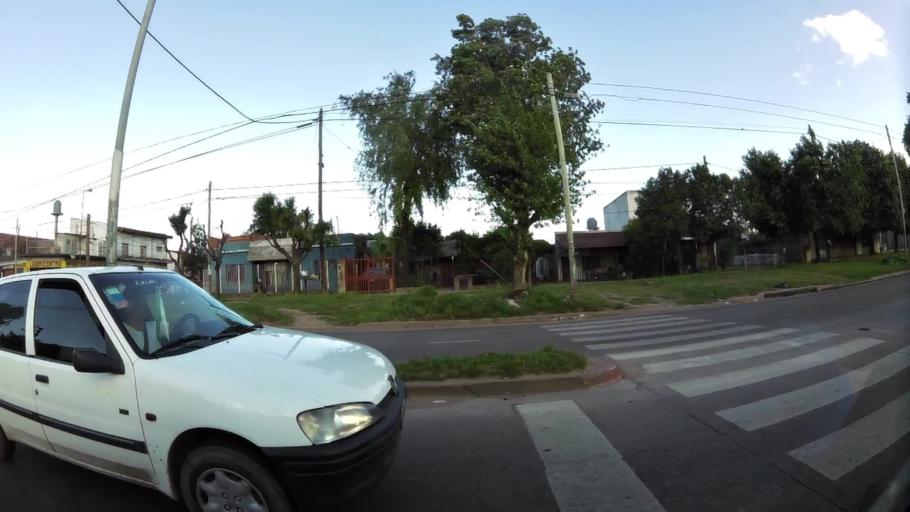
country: AR
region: Buenos Aires
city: Ituzaingo
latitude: -34.6969
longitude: -58.6384
